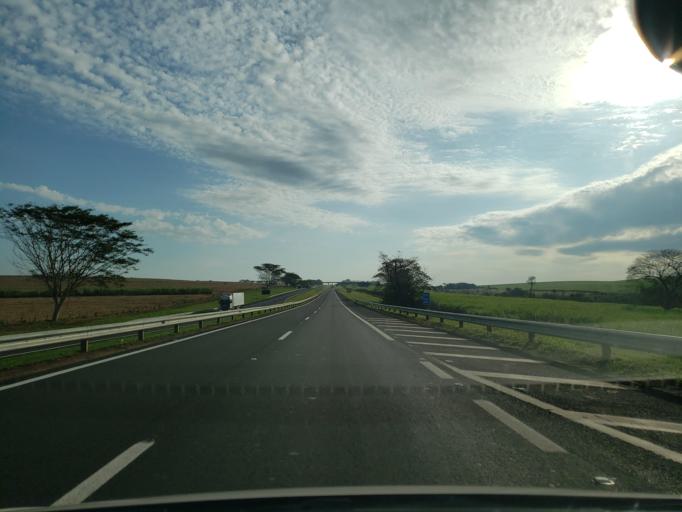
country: BR
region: Sao Paulo
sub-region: Valparaiso
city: Valparaiso
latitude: -21.2057
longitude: -50.7800
